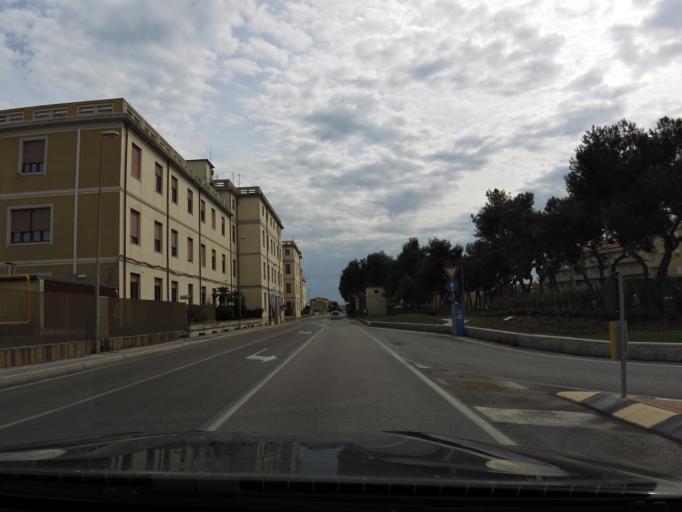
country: IT
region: The Marches
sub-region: Provincia di Macerata
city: Porto Potenza Picena
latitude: 43.3702
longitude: 13.6928
